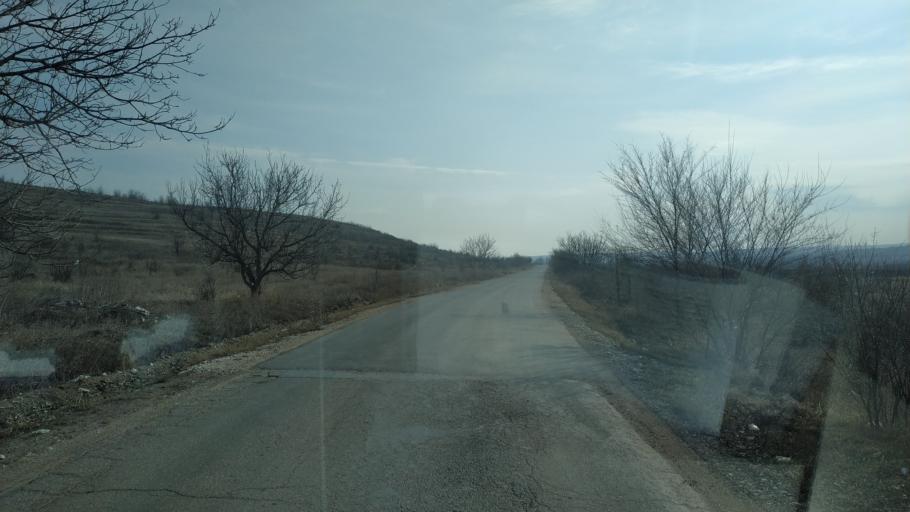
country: MD
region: Chisinau
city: Singera
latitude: 46.9226
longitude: 29.0932
